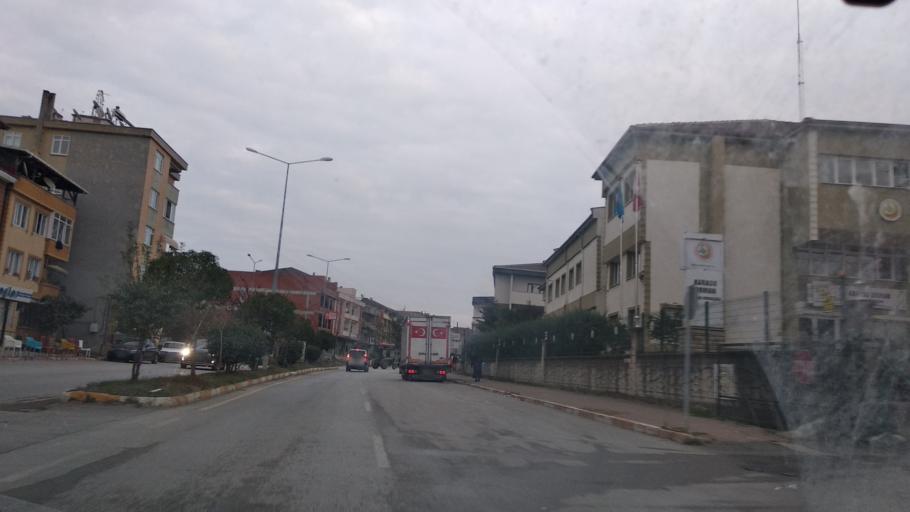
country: TR
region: Sakarya
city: Karasu
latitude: 41.0949
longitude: 30.6859
